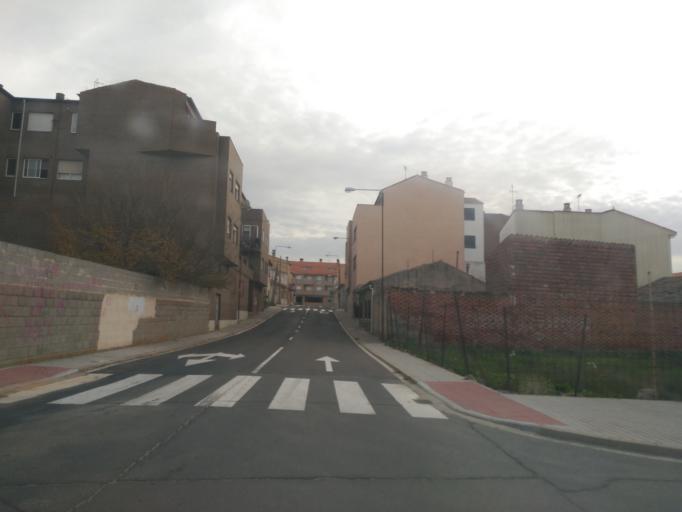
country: ES
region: Castille and Leon
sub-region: Provincia de Salamanca
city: Salamanca
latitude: 40.9564
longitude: -5.6817
